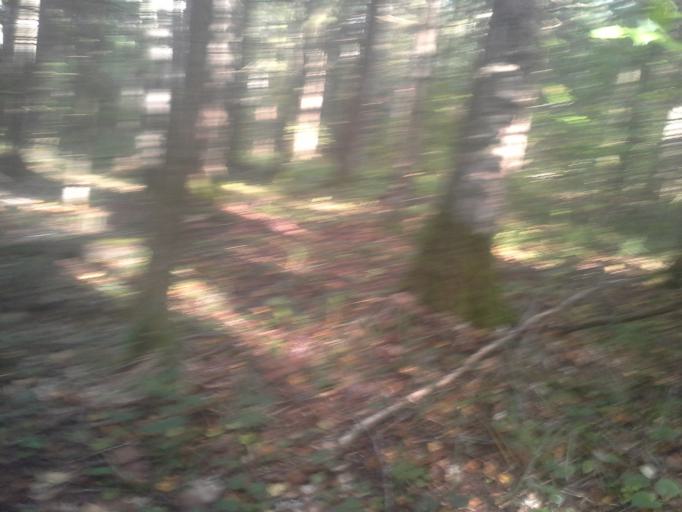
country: RU
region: Moskovskaya
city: Kievskij
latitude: 55.3614
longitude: 36.8985
